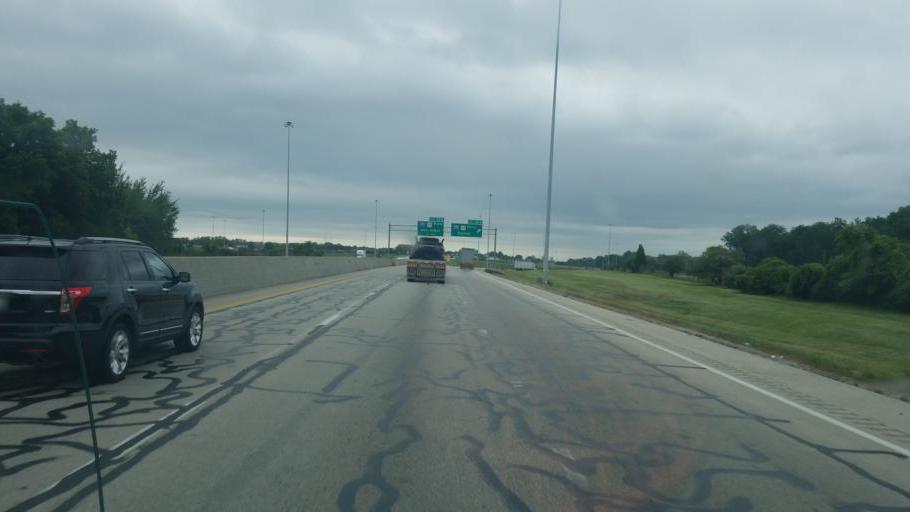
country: US
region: Ohio
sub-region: Lucas County
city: Maumee
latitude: 41.5494
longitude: -83.6917
